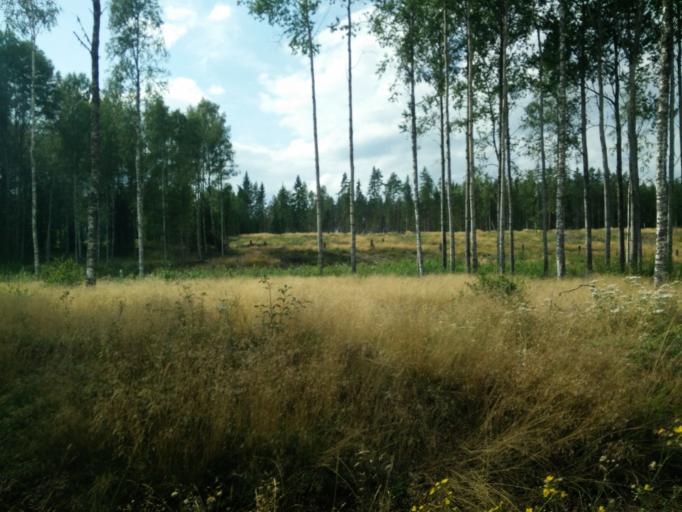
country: SE
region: Vaermland
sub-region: Hagfors Kommun
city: Hagfors
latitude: 59.9916
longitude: 13.5655
